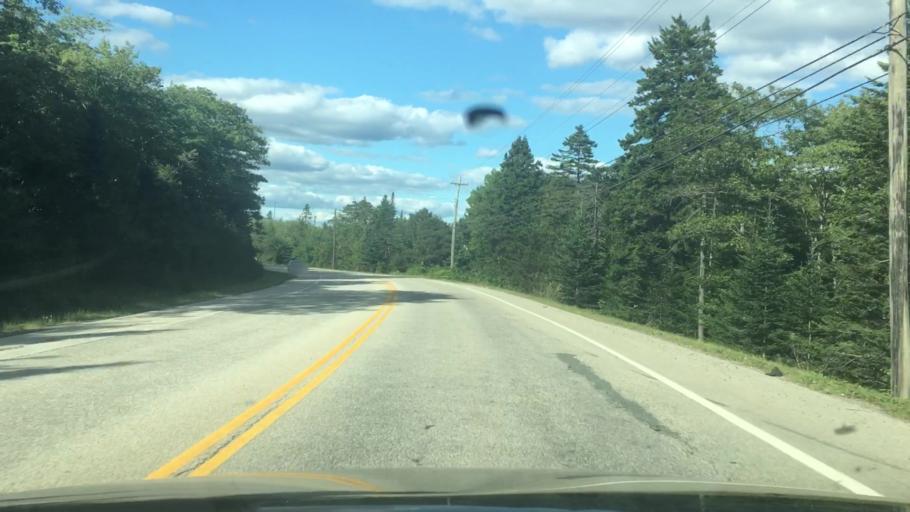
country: CA
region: Nova Scotia
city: Halifax
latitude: 44.6104
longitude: -63.6701
